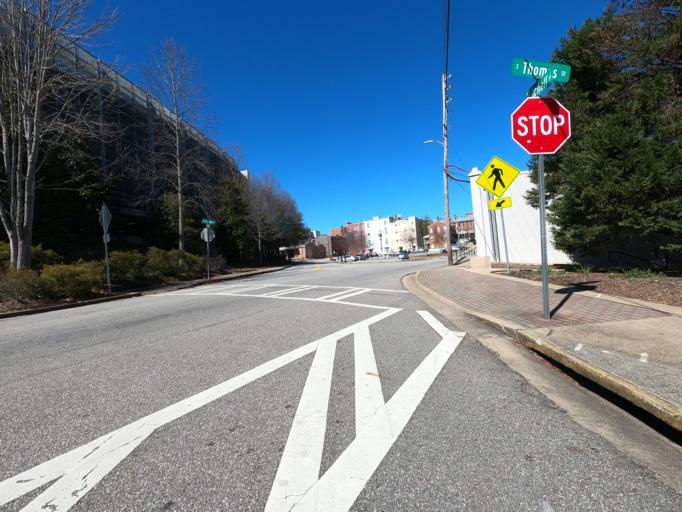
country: US
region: Georgia
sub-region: Clarke County
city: Athens
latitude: 33.9565
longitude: -83.3722
